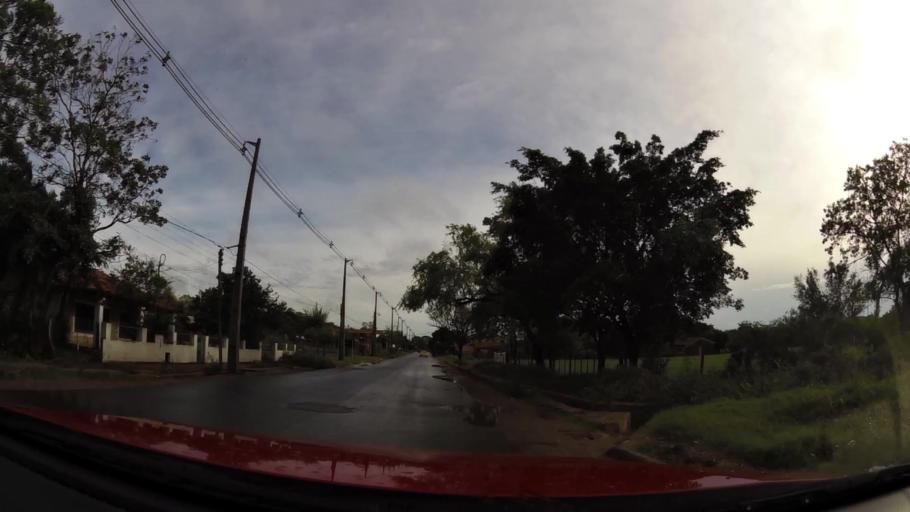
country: PY
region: Central
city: Limpio
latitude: -25.2022
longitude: -57.5033
